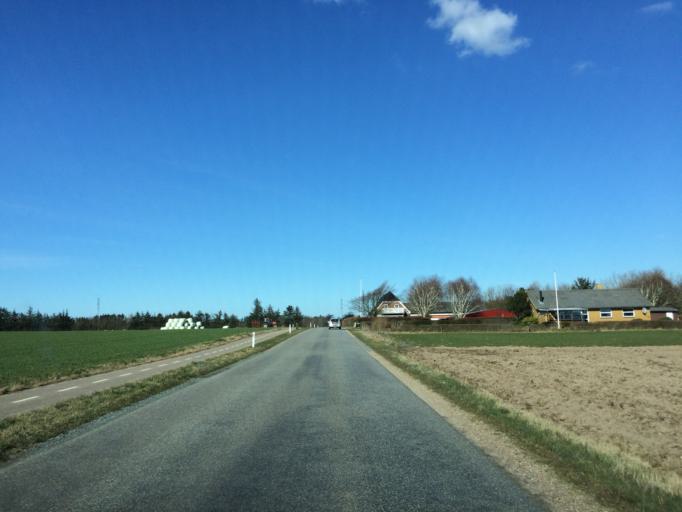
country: DK
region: South Denmark
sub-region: Varde Kommune
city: Oksbol
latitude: 55.7278
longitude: 8.2674
